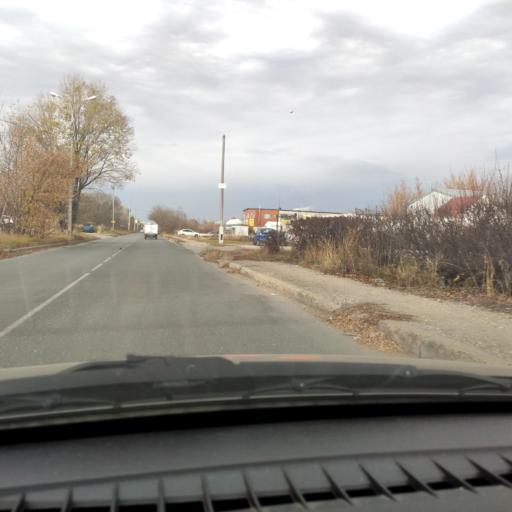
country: RU
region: Samara
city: Tol'yatti
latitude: 53.5547
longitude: 49.3186
